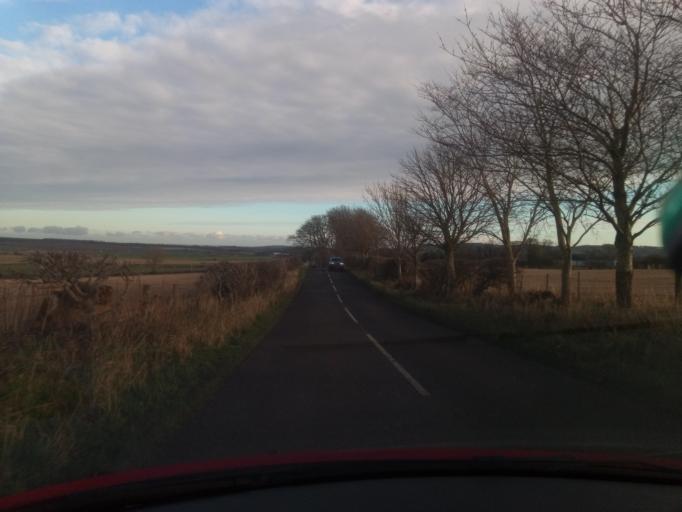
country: GB
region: Scotland
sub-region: The Scottish Borders
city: Chirnside
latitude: 55.8433
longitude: -2.1888
